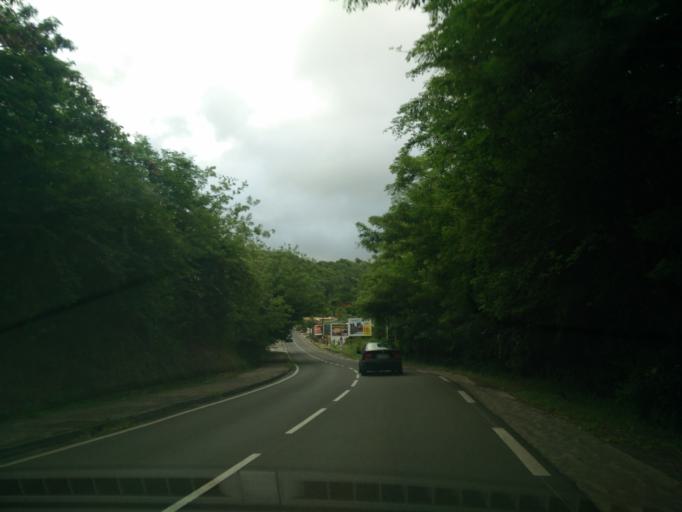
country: MQ
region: Martinique
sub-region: Martinique
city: Le Marin
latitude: 14.4730
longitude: -60.8589
